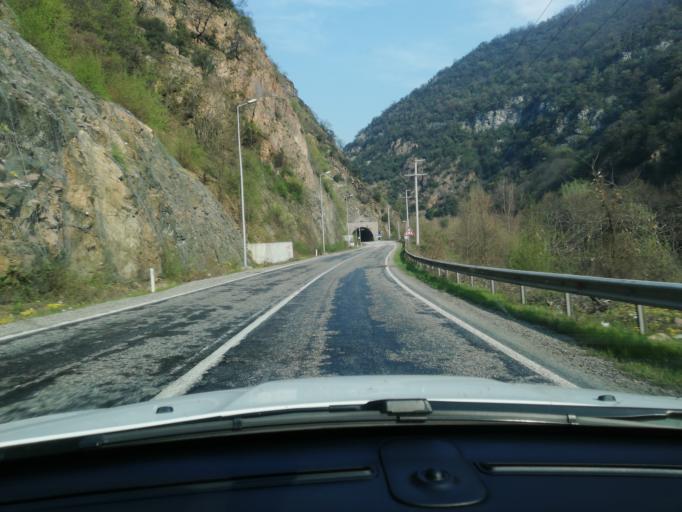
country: TR
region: Karabuk
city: Yenice
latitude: 41.1594
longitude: 32.4598
